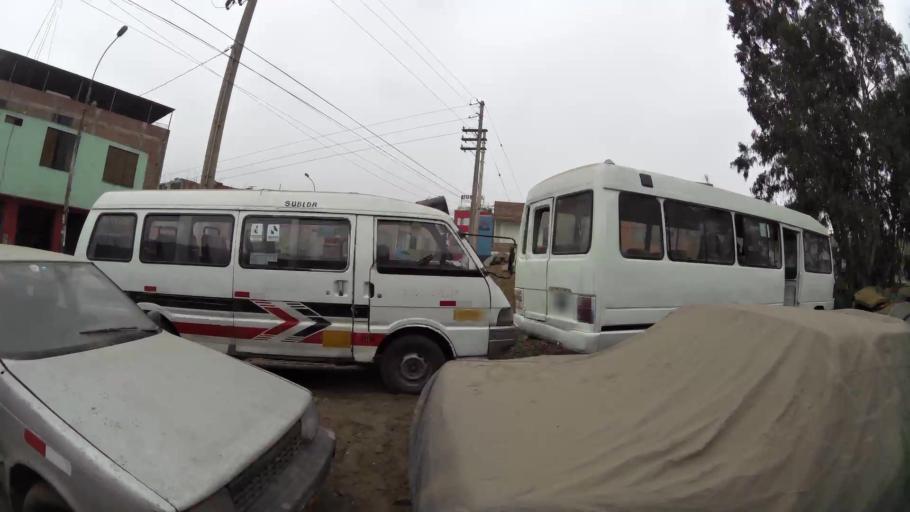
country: PE
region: Lima
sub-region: Lima
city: Surco
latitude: -12.1761
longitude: -76.9662
